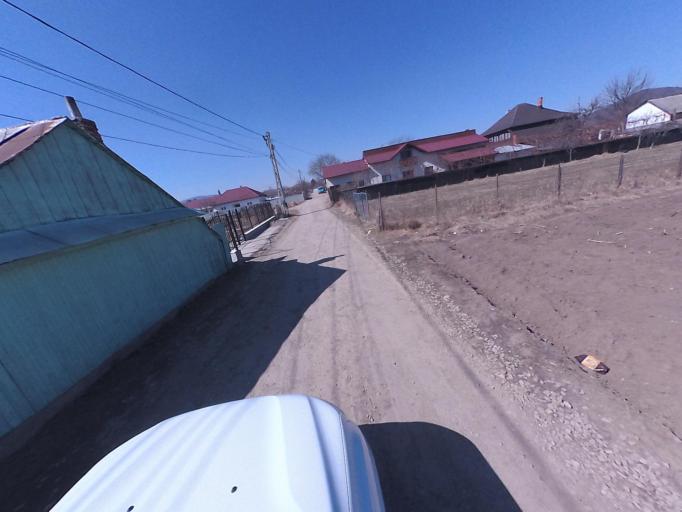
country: RO
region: Neamt
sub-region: Oras Targu Neamt
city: Humulesti
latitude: 47.1929
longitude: 26.3528
